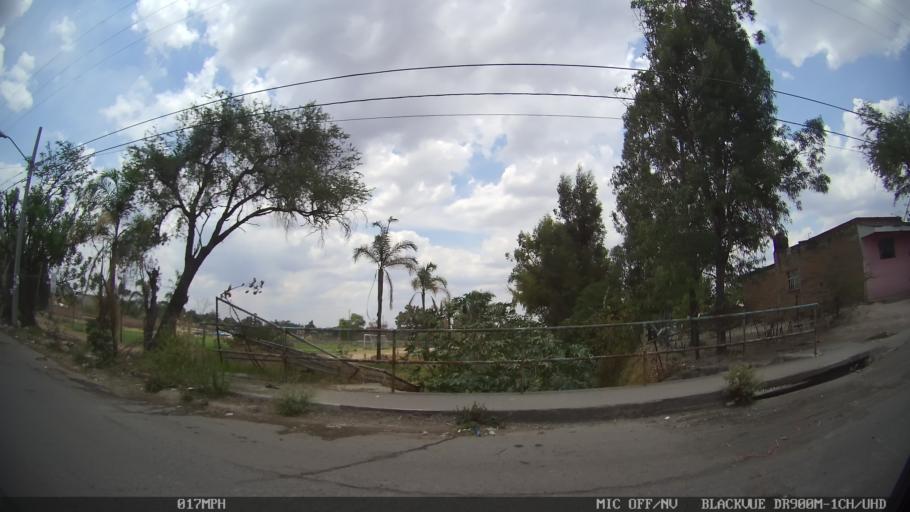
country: MX
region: Jalisco
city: Tonala
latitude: 20.6589
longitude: -103.2263
